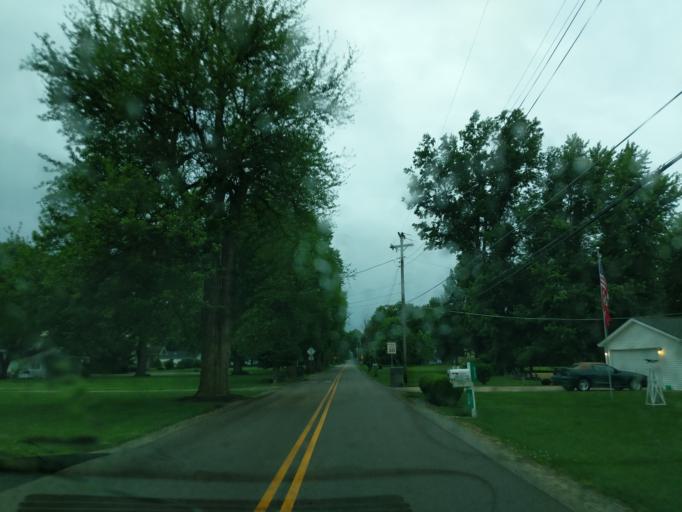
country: US
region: Indiana
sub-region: Madison County
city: Chesterfield
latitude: 40.0991
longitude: -85.6146
